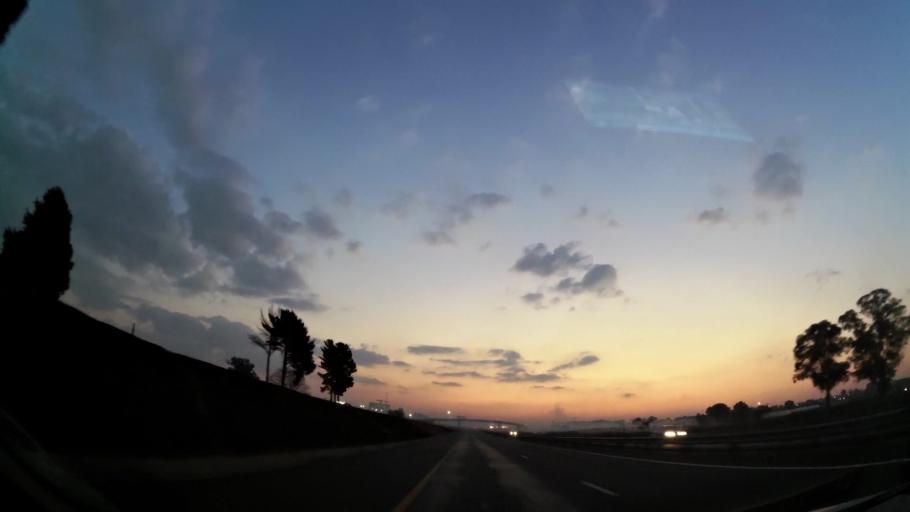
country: ZA
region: Gauteng
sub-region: Ekurhuleni Metropolitan Municipality
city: Springs
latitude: -26.2763
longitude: 28.3853
